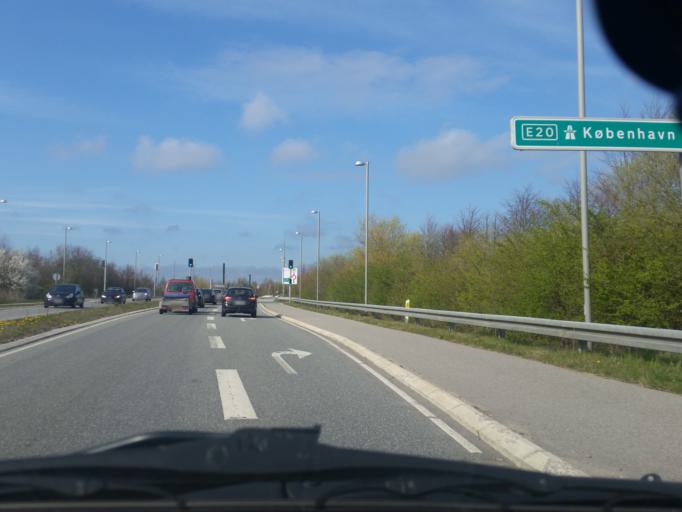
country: DK
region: Zealand
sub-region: Soro Kommune
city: Soro
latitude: 55.4584
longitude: 11.5620
